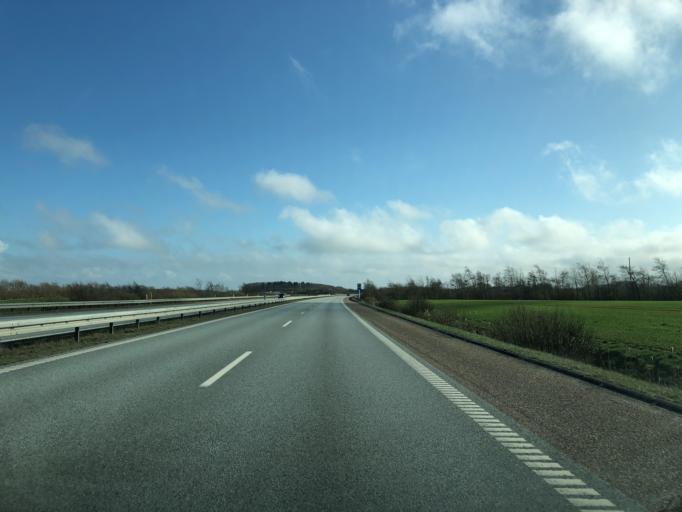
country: DK
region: North Denmark
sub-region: Hjorring Kommune
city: Hjorring
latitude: 57.4648
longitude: 10.0462
